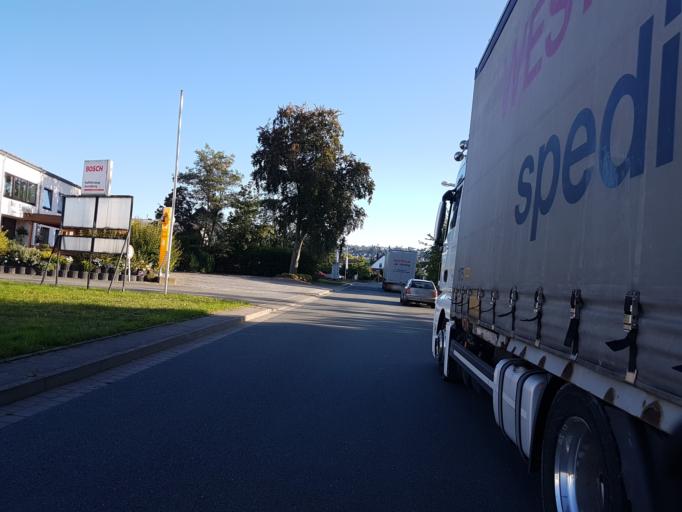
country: DE
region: North Rhine-Westphalia
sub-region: Regierungsbezirk Detmold
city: Vlotho
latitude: 52.1782
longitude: 8.8674
